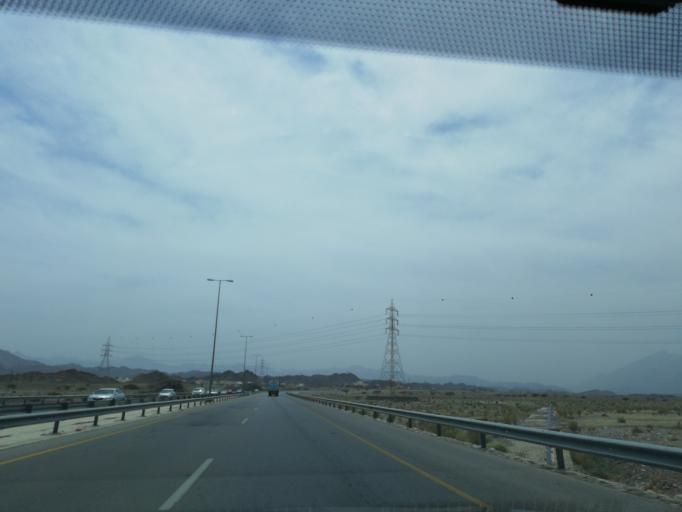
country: OM
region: Muhafazat ad Dakhiliyah
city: Sufalat Sama'il
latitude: 23.2694
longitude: 57.9369
